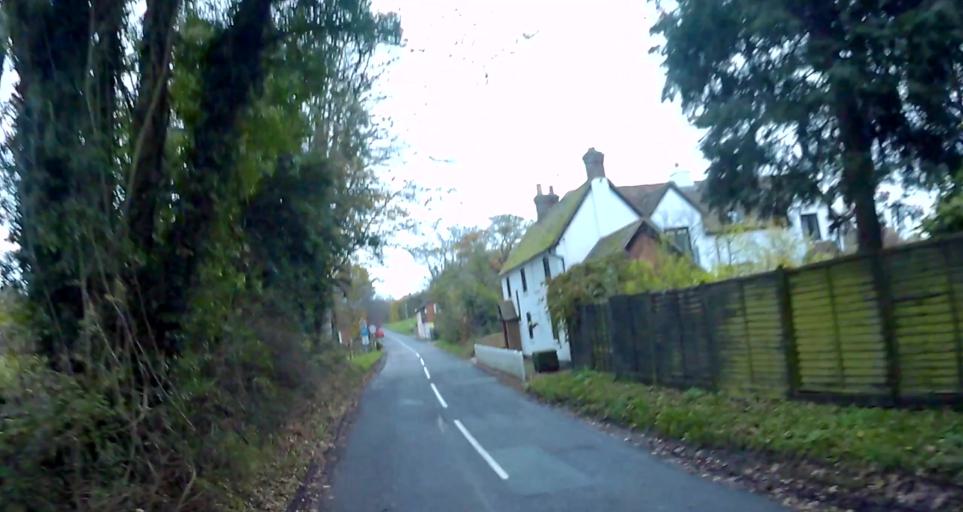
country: GB
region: England
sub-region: Hampshire
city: Odiham
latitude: 51.2498
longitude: -0.9370
